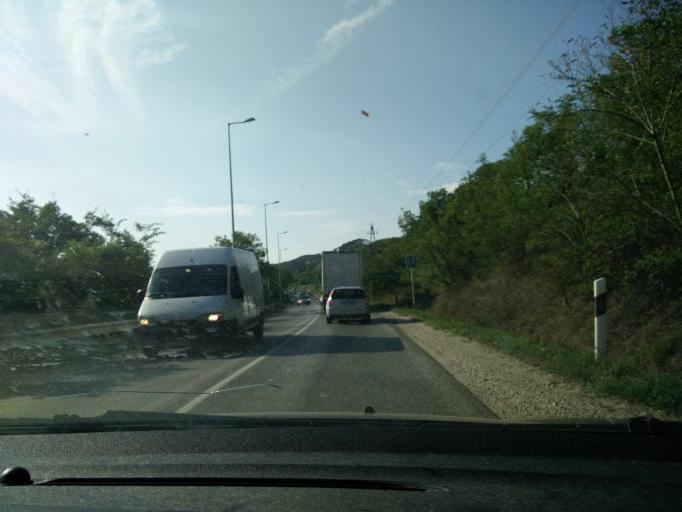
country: HU
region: Pest
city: Pilisszentivan
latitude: 47.6172
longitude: 18.8841
